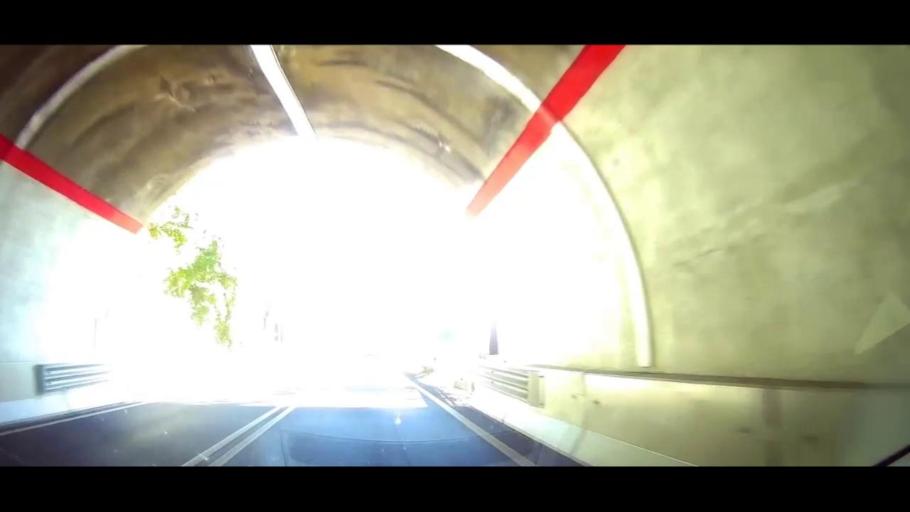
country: IT
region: Calabria
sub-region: Provincia di Cosenza
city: Spezzano della Sila
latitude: 39.2965
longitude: 16.3445
